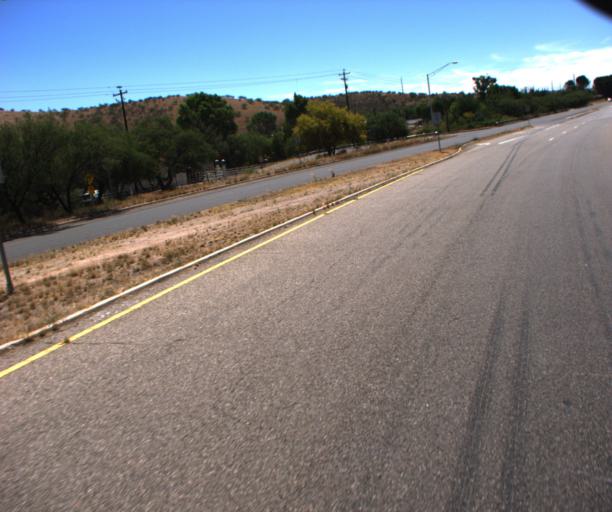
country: US
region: Arizona
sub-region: Santa Cruz County
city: Nogales
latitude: 31.3941
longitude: -110.9568
